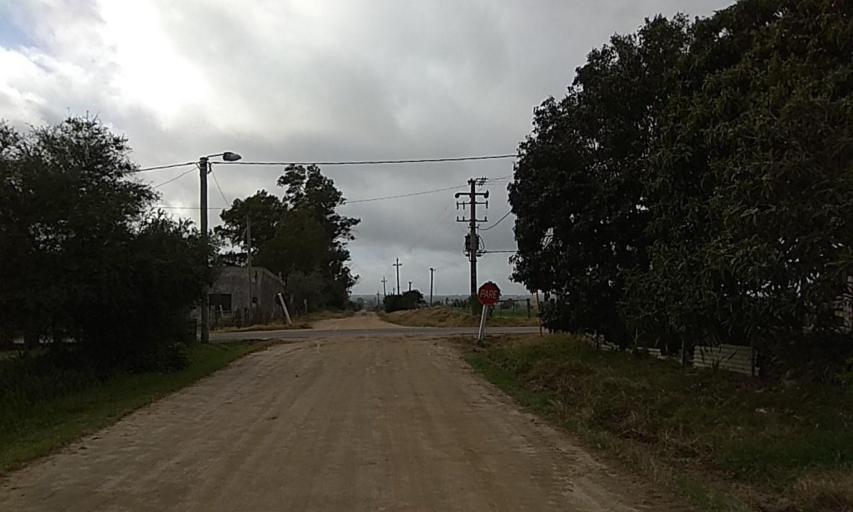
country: UY
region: Florida
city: Florida
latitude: -34.0615
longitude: -56.2046
